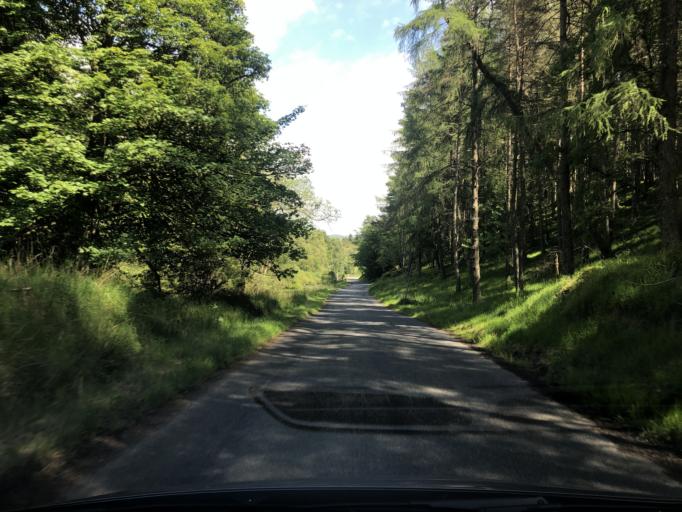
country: GB
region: Scotland
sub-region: Angus
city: Kirriemuir
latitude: 56.7338
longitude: -3.0202
